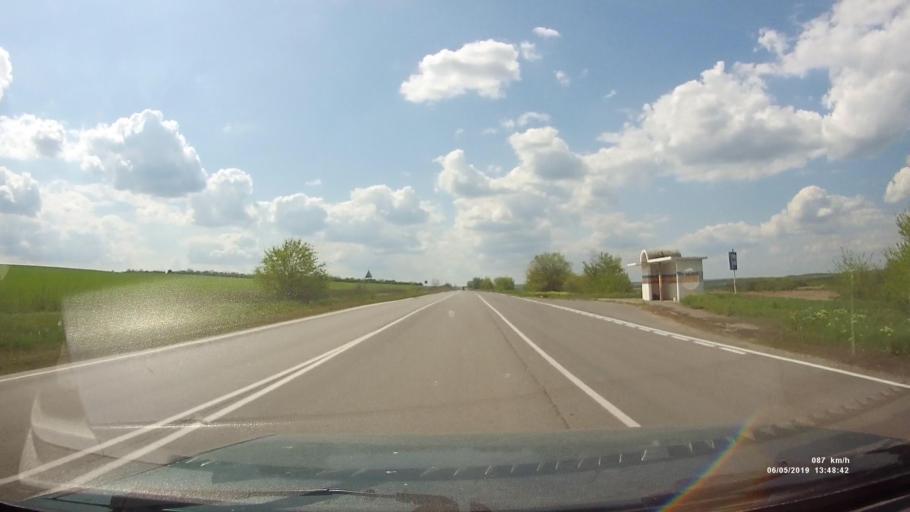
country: RU
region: Rostov
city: Melikhovskaya
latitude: 47.6586
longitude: 40.5386
